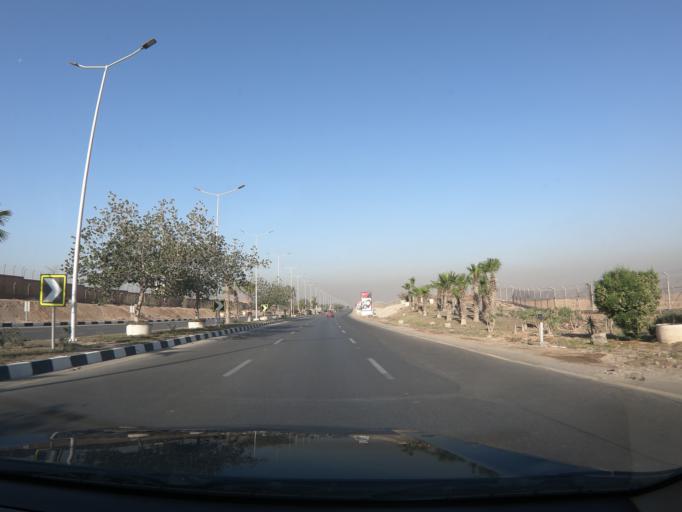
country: EG
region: Muhafazat al Qalyubiyah
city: Al Khankah
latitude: 30.0908
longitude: 31.4042
